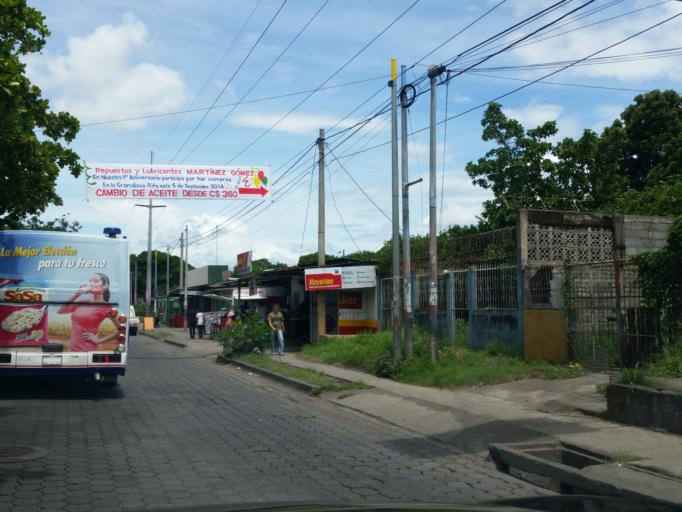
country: NI
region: Managua
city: Managua
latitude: 12.1274
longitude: -86.2372
